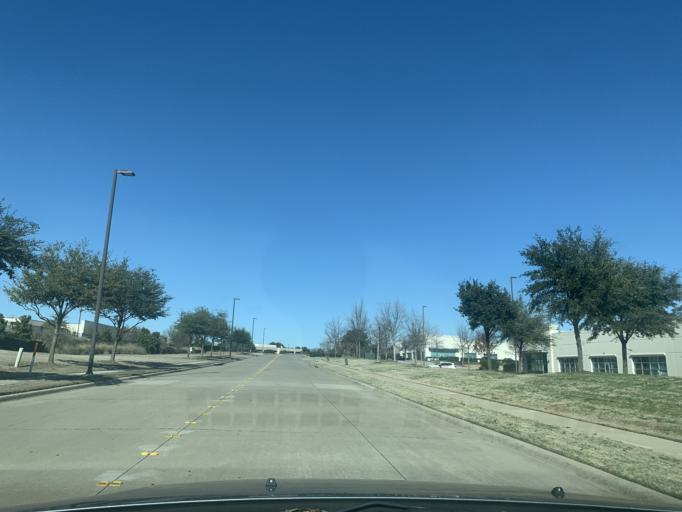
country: US
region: Texas
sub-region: Denton County
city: The Colony
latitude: 33.0646
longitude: -96.8093
